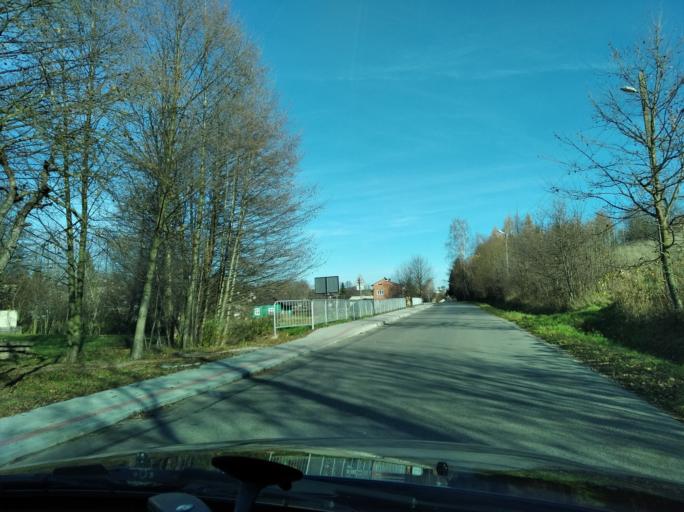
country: PL
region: Subcarpathian Voivodeship
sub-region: Powiat rzeszowski
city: Lutoryz
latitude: 49.9632
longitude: 21.8959
